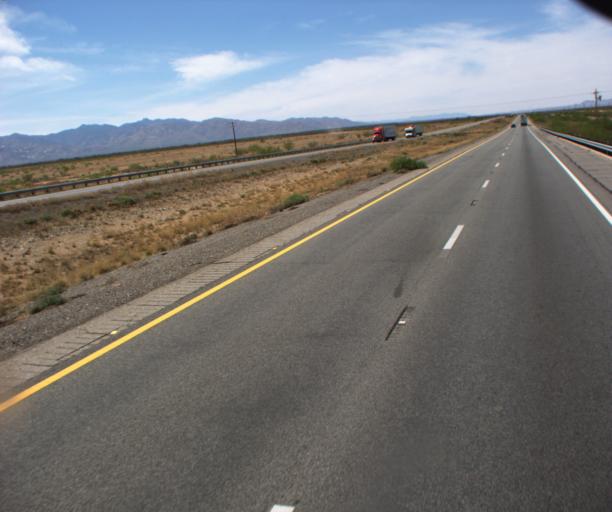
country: US
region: Arizona
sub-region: Cochise County
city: Willcox
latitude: 32.2975
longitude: -109.3541
